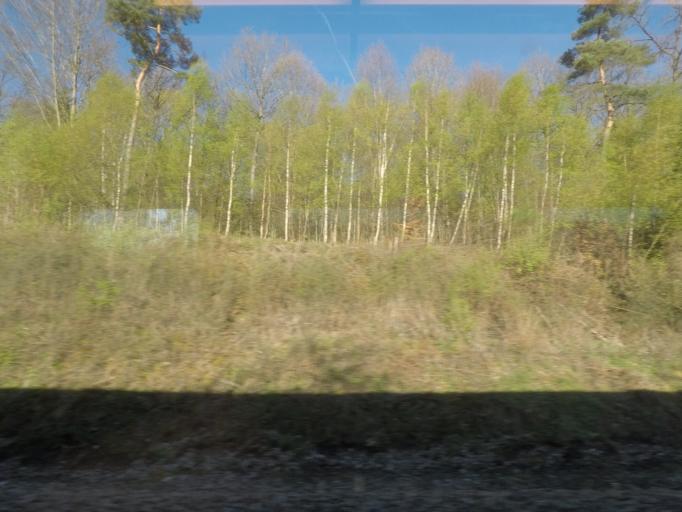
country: BE
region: Wallonia
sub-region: Province du Luxembourg
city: Tellin
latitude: 50.0692
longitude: 5.2664
